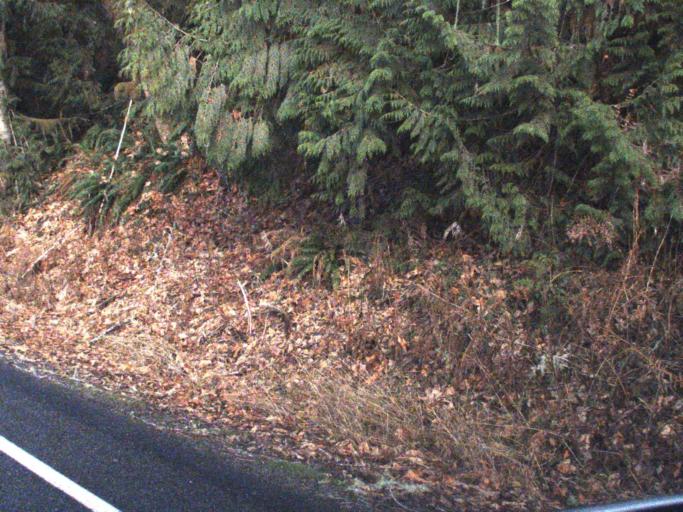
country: US
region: Washington
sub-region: Snohomish County
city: Darrington
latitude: 48.3924
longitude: -121.5500
